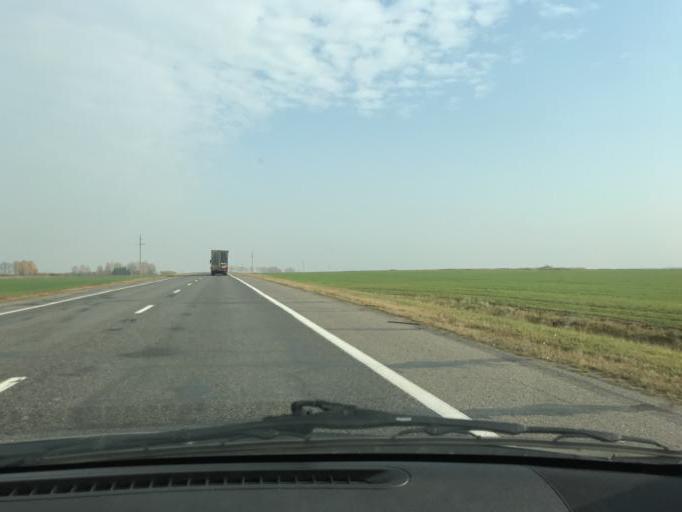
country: BY
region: Vitebsk
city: Chashniki
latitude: 55.0109
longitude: 29.1623
